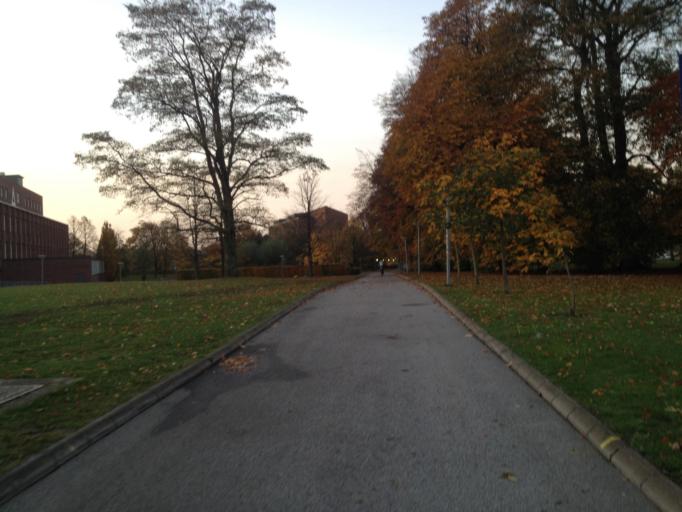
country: SE
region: Skane
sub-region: Lunds Kommun
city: Lund
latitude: 55.7146
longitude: 13.2118
